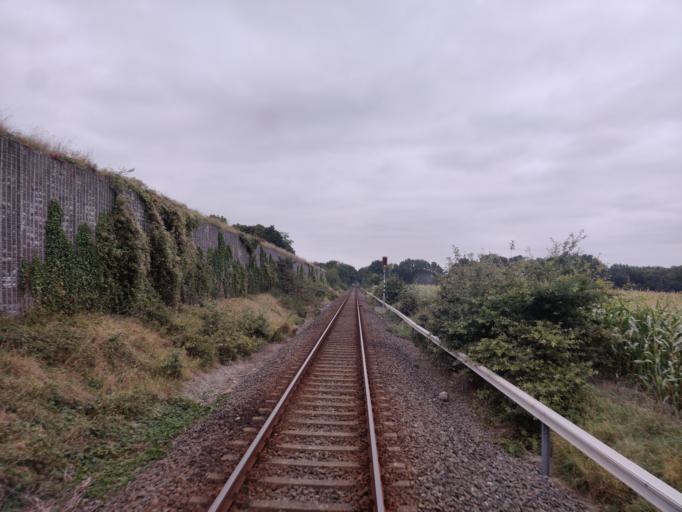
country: DE
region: Lower Saxony
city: Stade
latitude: 53.5721
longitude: 9.4744
